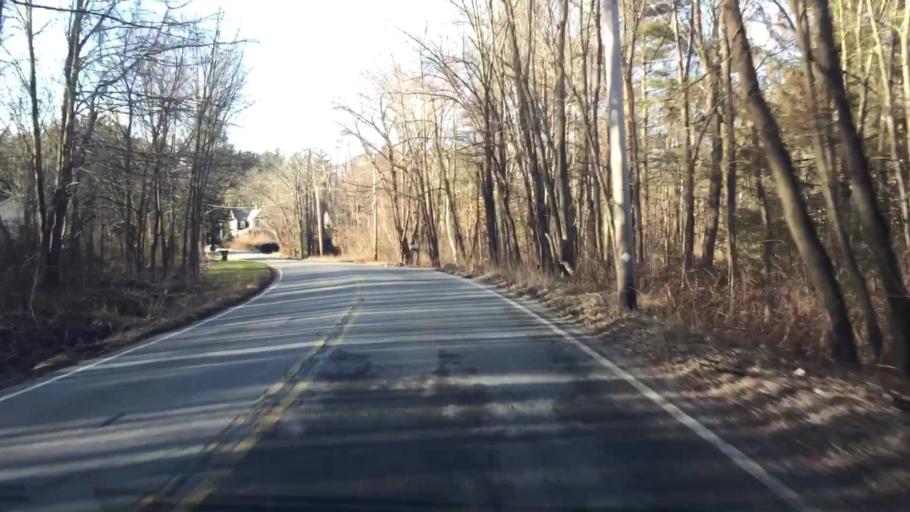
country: US
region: Massachusetts
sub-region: Worcester County
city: Princeton
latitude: 42.4391
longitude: -71.8218
